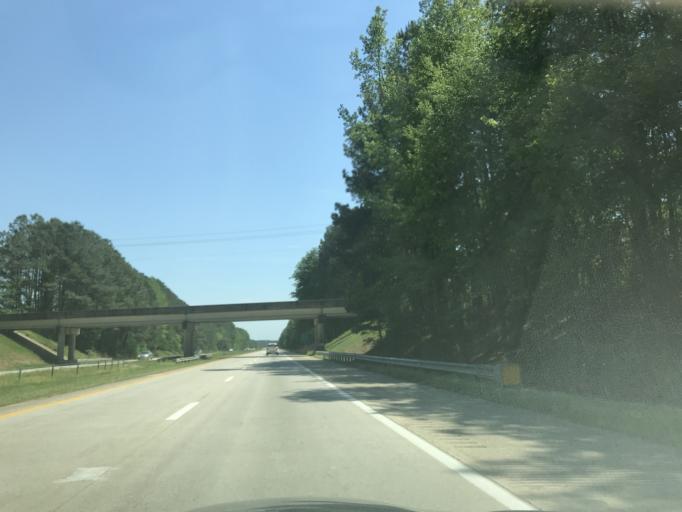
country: US
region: North Carolina
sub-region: Johnston County
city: Benson
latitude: 35.5329
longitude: -78.5699
